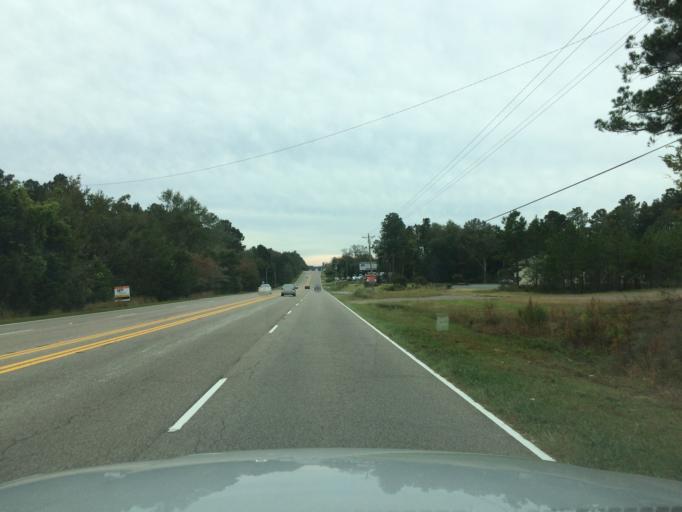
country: US
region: South Carolina
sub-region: Aiken County
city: New Ellenton
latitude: 33.4332
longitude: -81.6861
